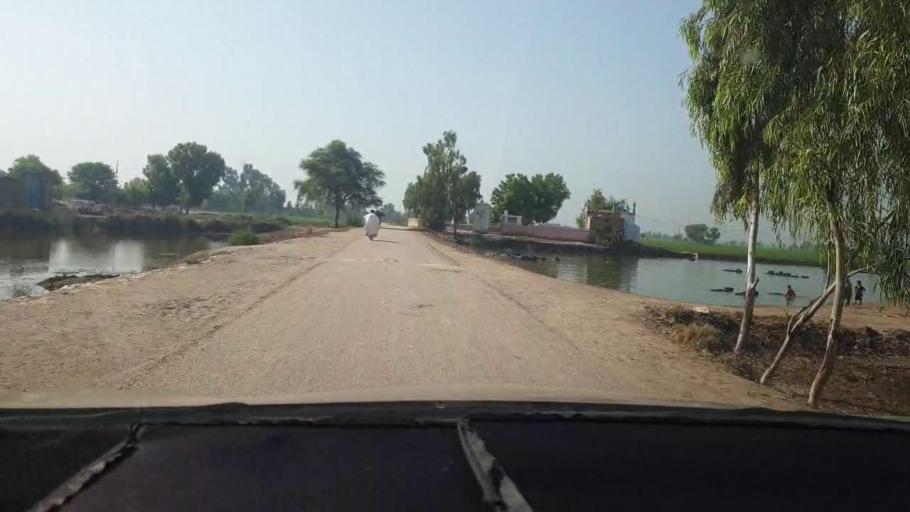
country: PK
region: Sindh
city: Kambar
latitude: 27.6014
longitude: 68.0933
